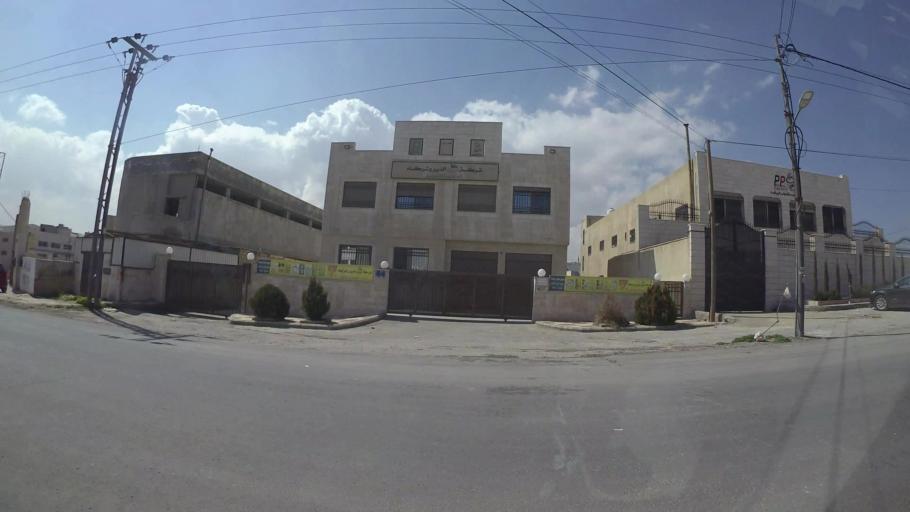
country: JO
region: Zarqa
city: Russeifa
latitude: 31.9930
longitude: 36.0123
